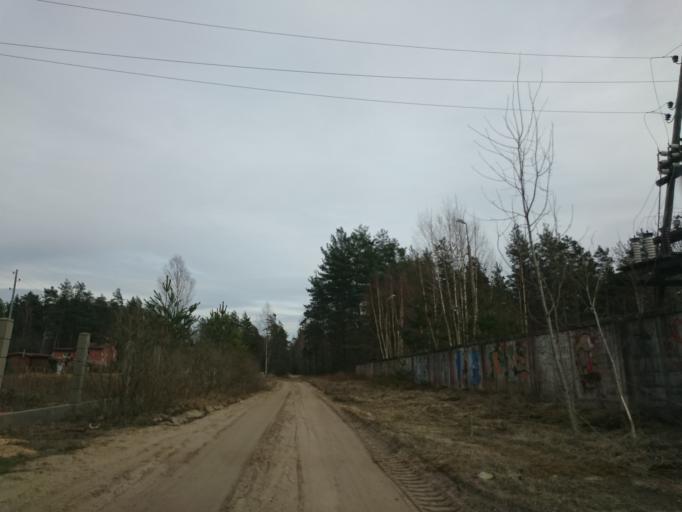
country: LV
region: Garkalne
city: Garkalne
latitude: 57.0141
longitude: 24.3965
